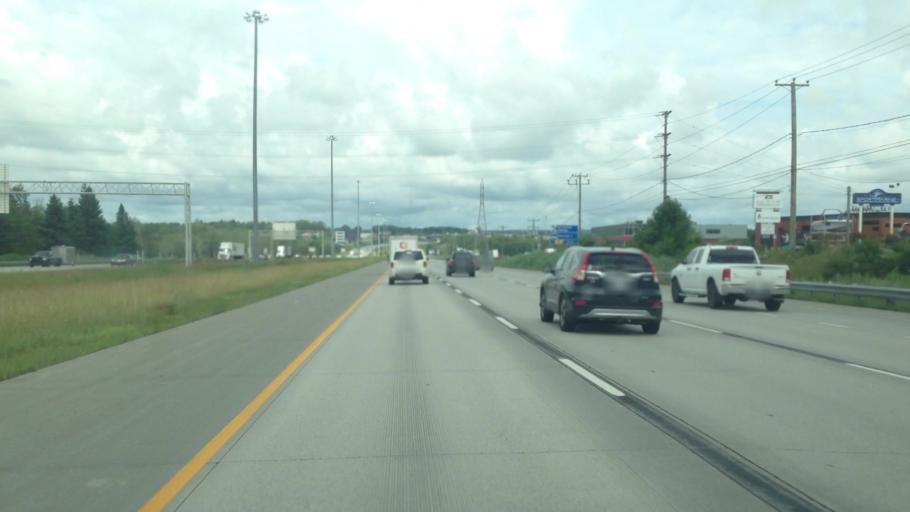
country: CA
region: Quebec
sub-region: Laurentides
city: Saint-Jerome
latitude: 45.7479
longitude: -74.0068
